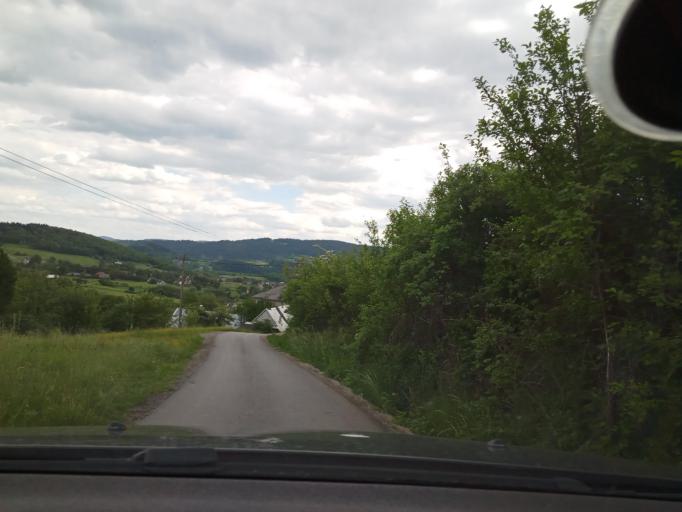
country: PL
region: Lesser Poland Voivodeship
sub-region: Powiat limanowski
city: Tymbark
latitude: 49.7701
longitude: 20.3363
